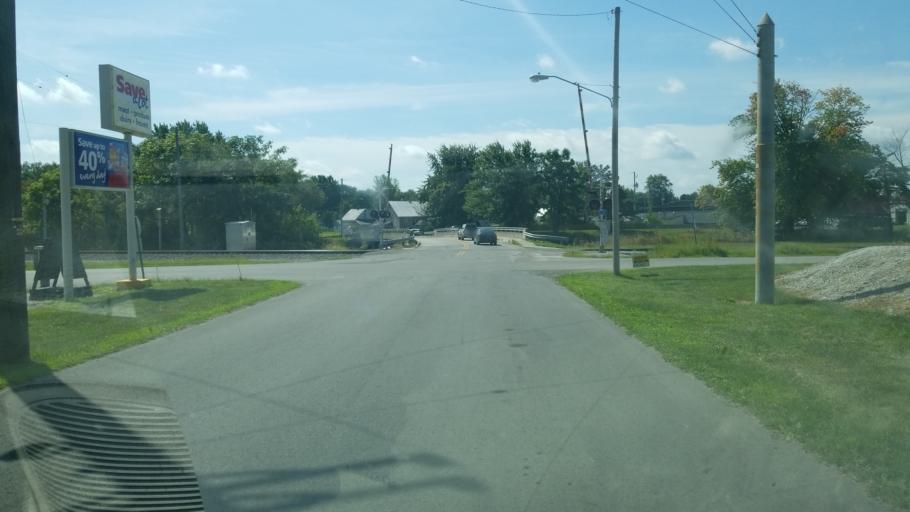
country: US
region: Ohio
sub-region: Hardin County
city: Kenton
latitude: 40.6441
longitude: -83.6069
